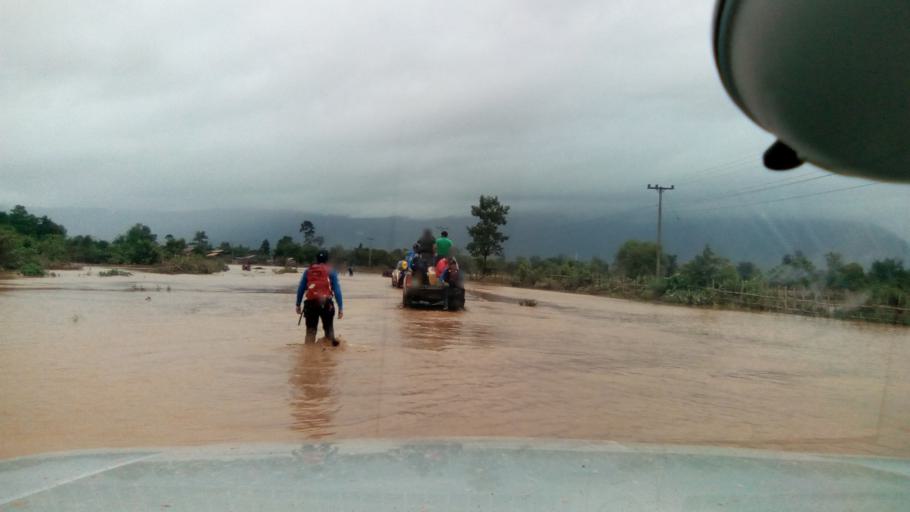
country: LA
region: Attapu
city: Attapu
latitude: 14.6977
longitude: 106.5319
